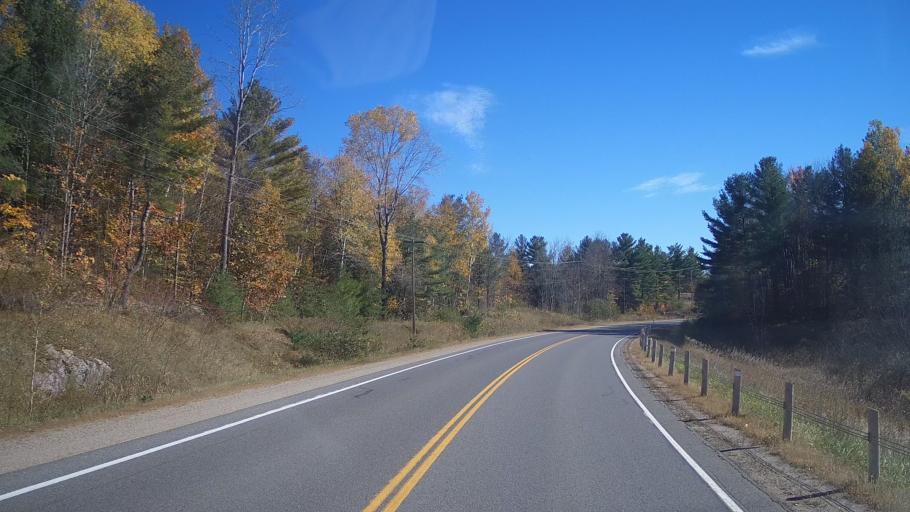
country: CA
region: Ontario
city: Skatepark
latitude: 44.6288
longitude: -76.7040
